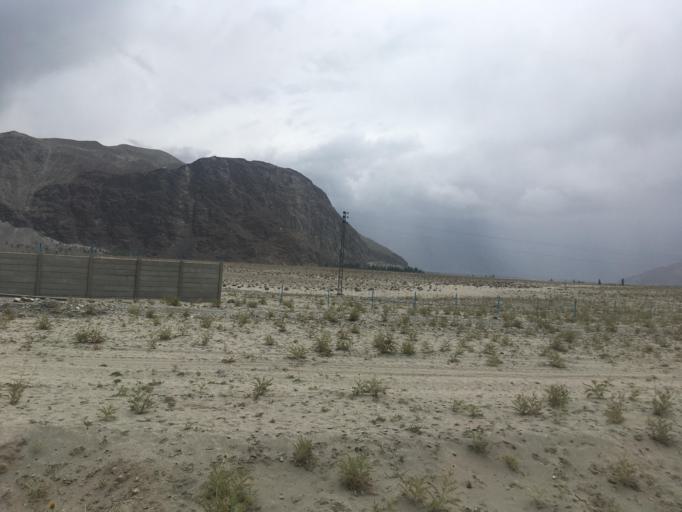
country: PK
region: Gilgit-Baltistan
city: Skardu
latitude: 35.3166
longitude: 75.6573
